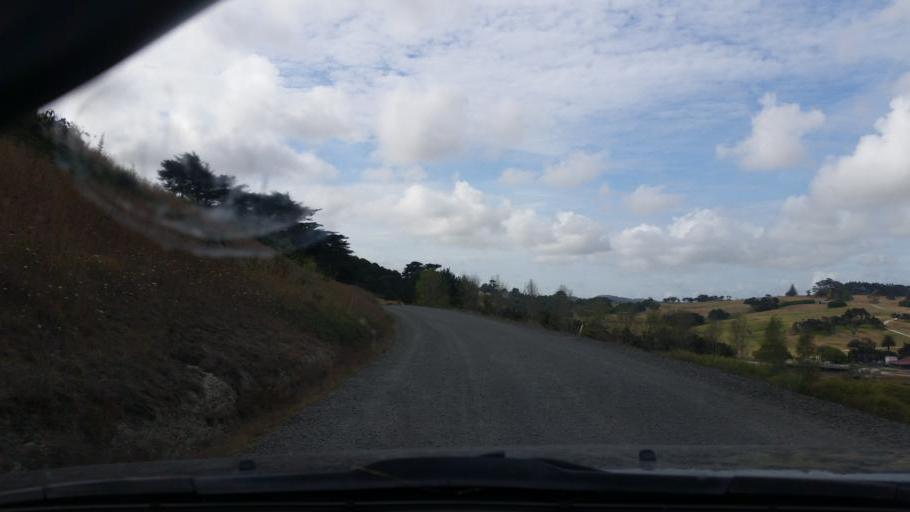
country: NZ
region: Northland
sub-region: Kaipara District
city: Dargaville
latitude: -35.9754
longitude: 173.9515
